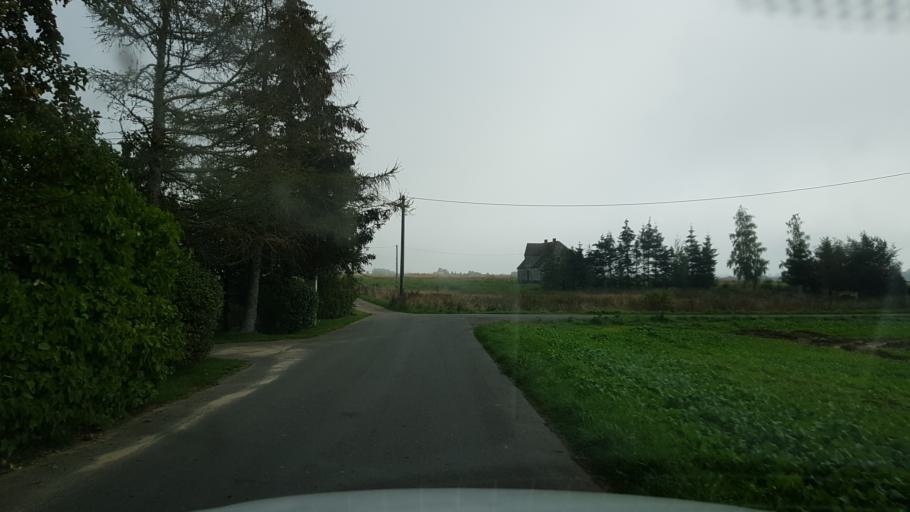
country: PL
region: West Pomeranian Voivodeship
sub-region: Powiat koszalinski
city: Mielno
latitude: 54.2299
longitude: 15.9448
